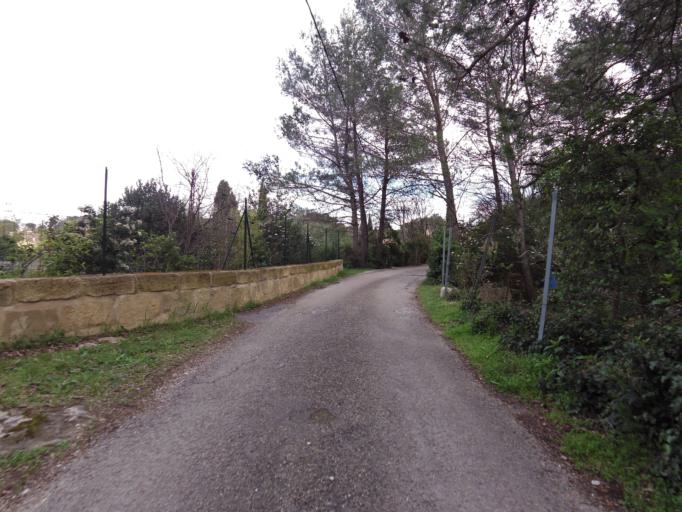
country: FR
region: Languedoc-Roussillon
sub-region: Departement du Gard
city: Aigues-Vives
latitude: 43.7380
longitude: 4.1676
